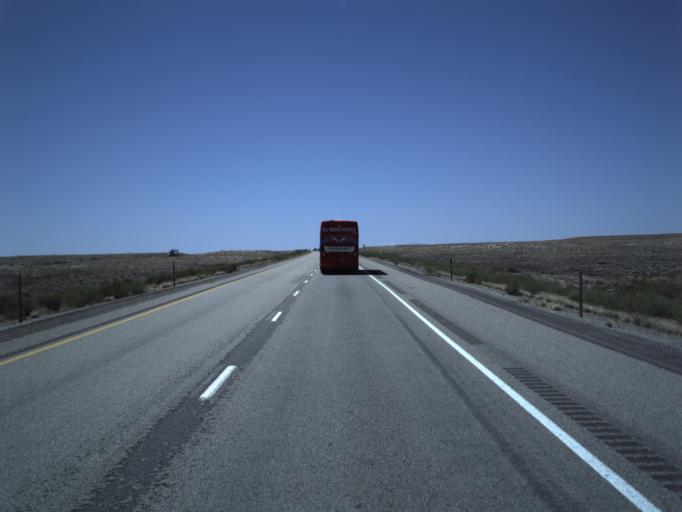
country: US
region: Utah
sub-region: Grand County
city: Moab
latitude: 38.9638
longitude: -109.3763
